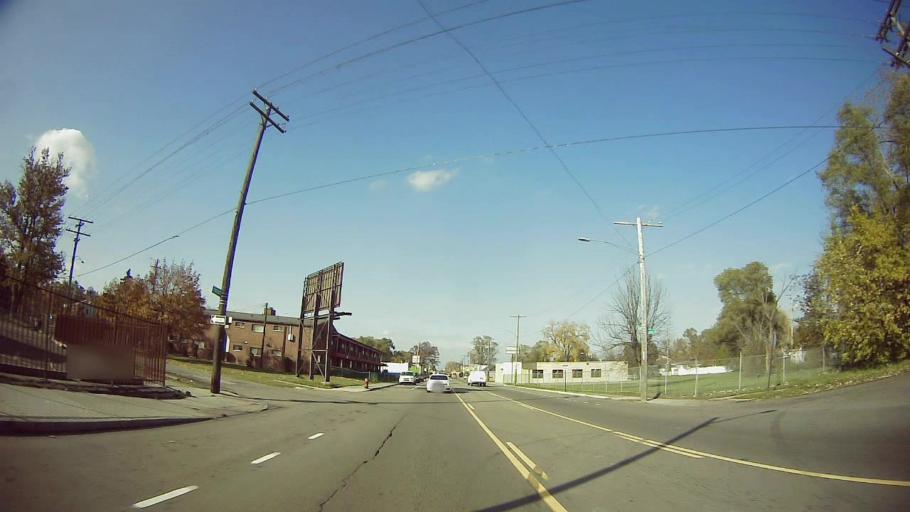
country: US
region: Michigan
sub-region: Oakland County
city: Hazel Park
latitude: 42.4377
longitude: -83.0771
